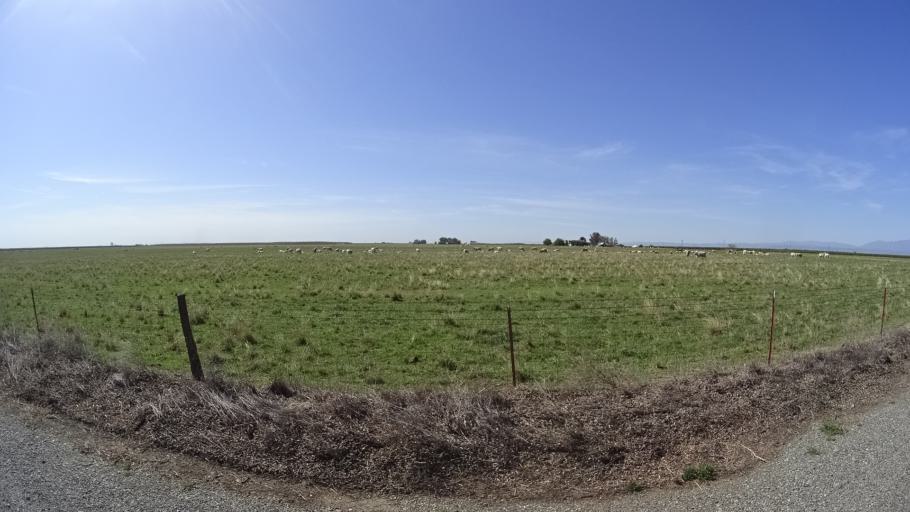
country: US
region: California
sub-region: Glenn County
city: Willows
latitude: 39.6238
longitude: -122.1508
